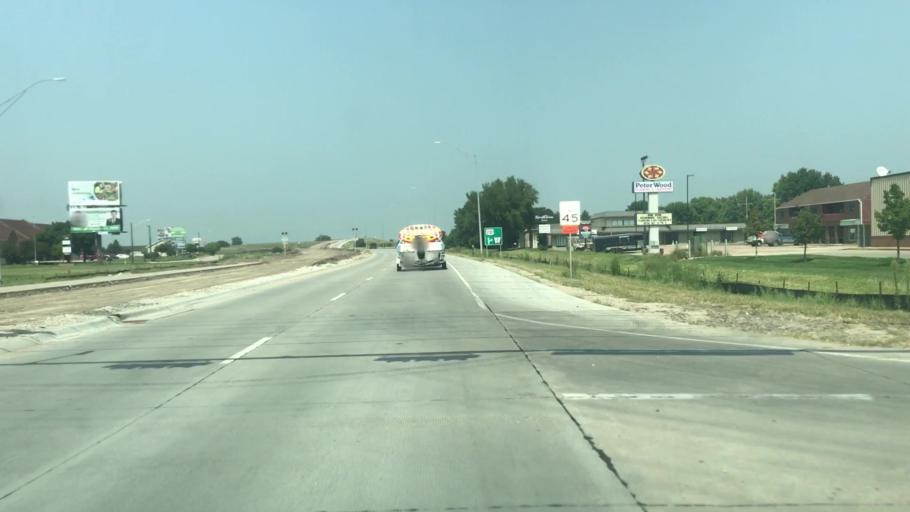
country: US
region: Nebraska
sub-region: Hall County
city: Grand Island
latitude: 40.9461
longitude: -98.3835
